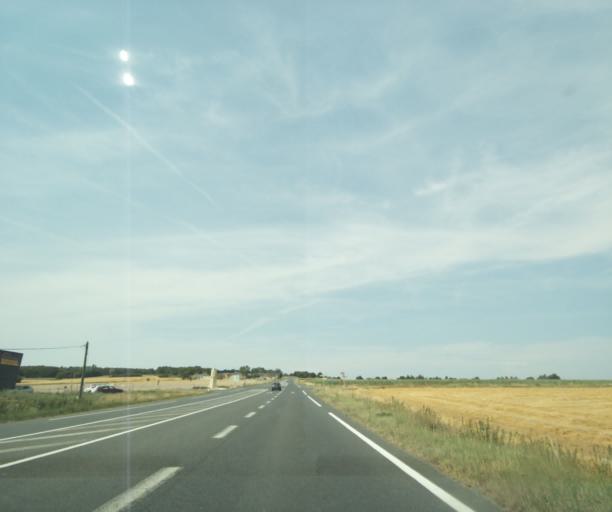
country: FR
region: Centre
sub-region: Departement d'Indre-et-Loire
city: La Celle-Saint-Avant
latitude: 47.0508
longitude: 0.6138
